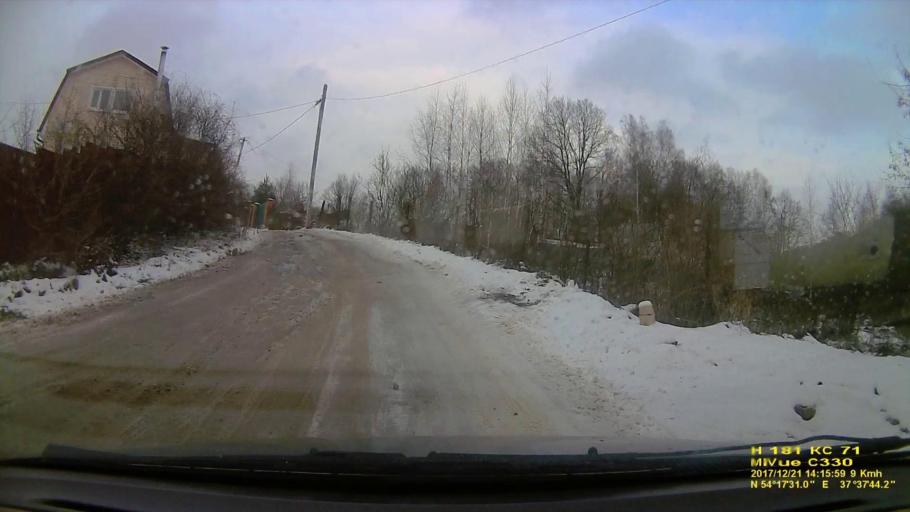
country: RU
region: Tula
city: Gorelki
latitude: 54.2920
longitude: 37.6290
